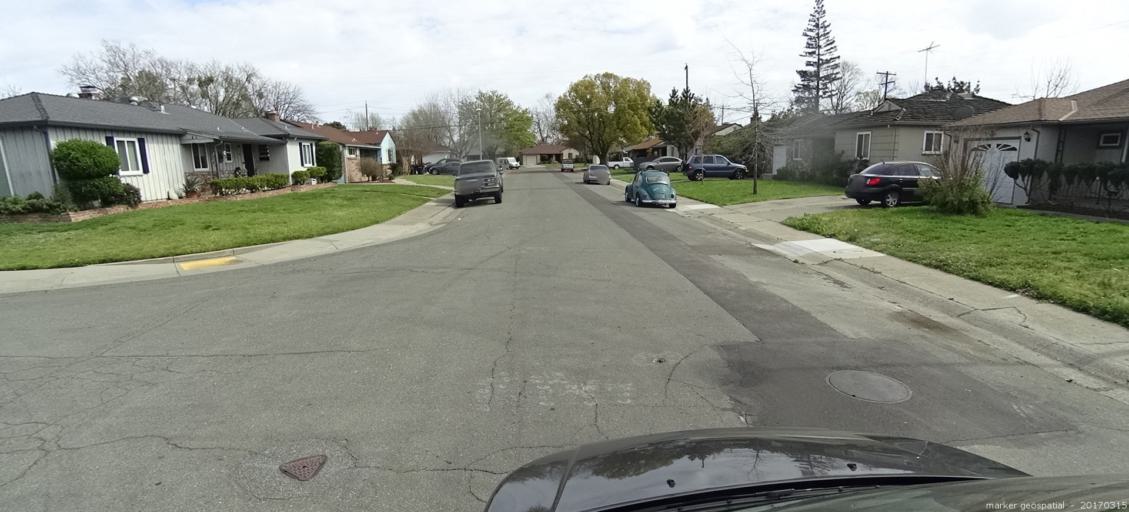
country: US
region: California
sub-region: Sacramento County
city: Parkway
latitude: 38.5230
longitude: -121.4812
